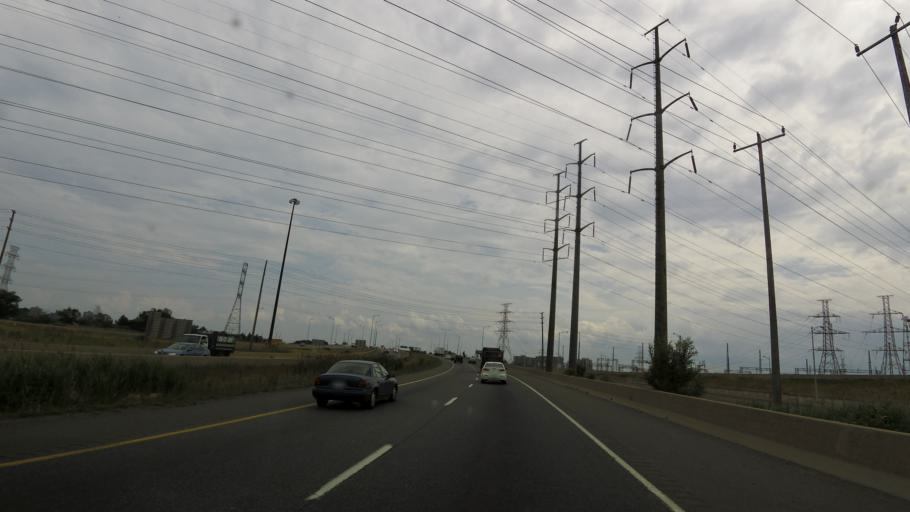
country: CA
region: Ontario
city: Burlington
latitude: 43.3346
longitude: -79.8294
